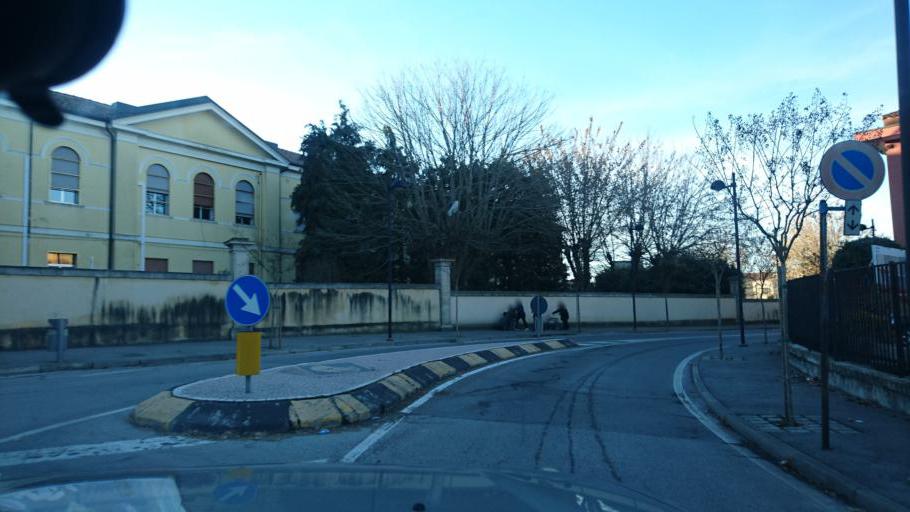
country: IT
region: Veneto
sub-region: Provincia di Rovigo
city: Adria
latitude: 45.0497
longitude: 12.0548
